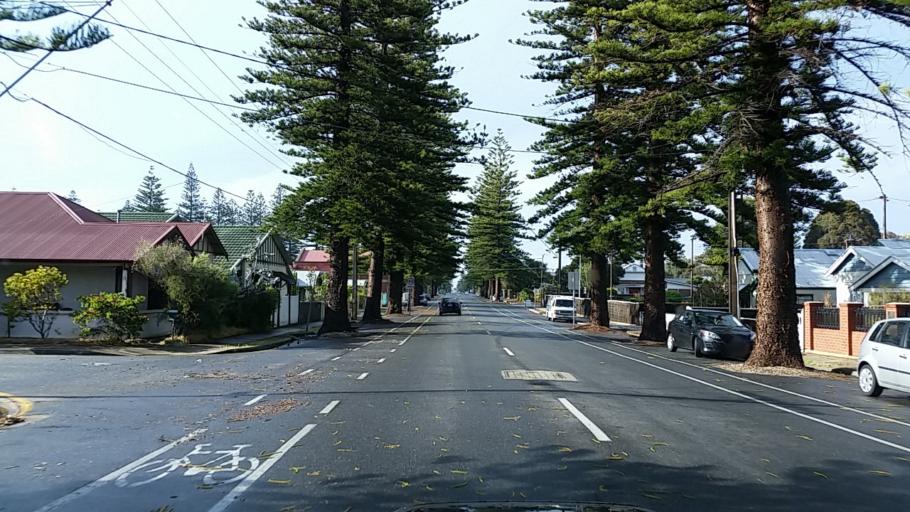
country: AU
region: South Australia
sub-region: Charles Sturt
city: Henley Beach
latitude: -34.9186
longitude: 138.4971
